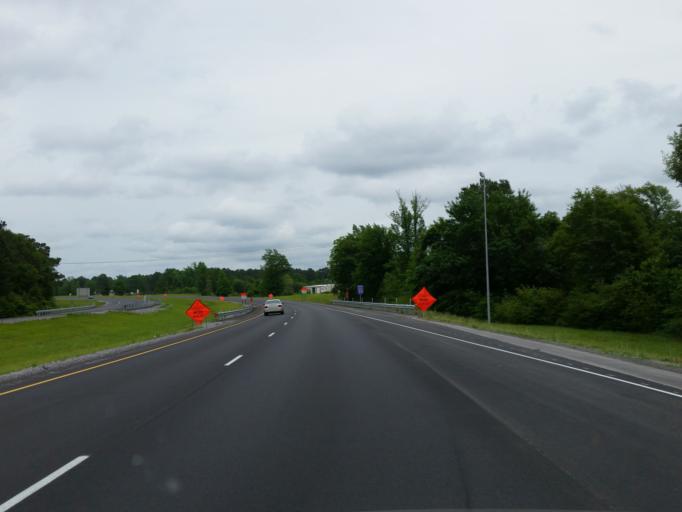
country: US
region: Mississippi
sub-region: Jones County
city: Sharon
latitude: 31.9090
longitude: -89.0114
